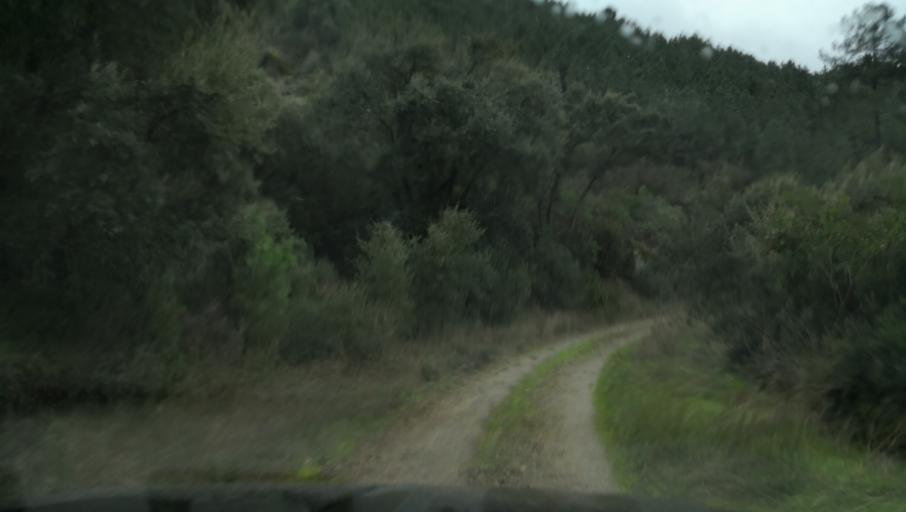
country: PT
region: Vila Real
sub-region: Vila Real
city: Vila Real
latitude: 41.2482
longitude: -7.7470
